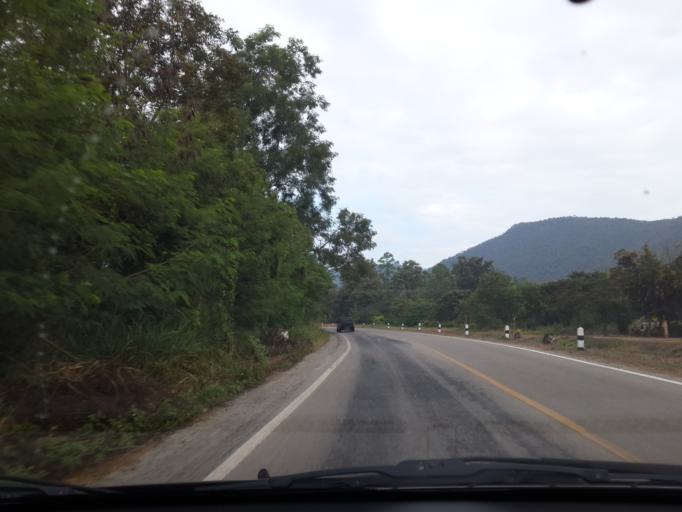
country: TH
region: Chiang Mai
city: San Sai
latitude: 18.9130
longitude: 99.1489
